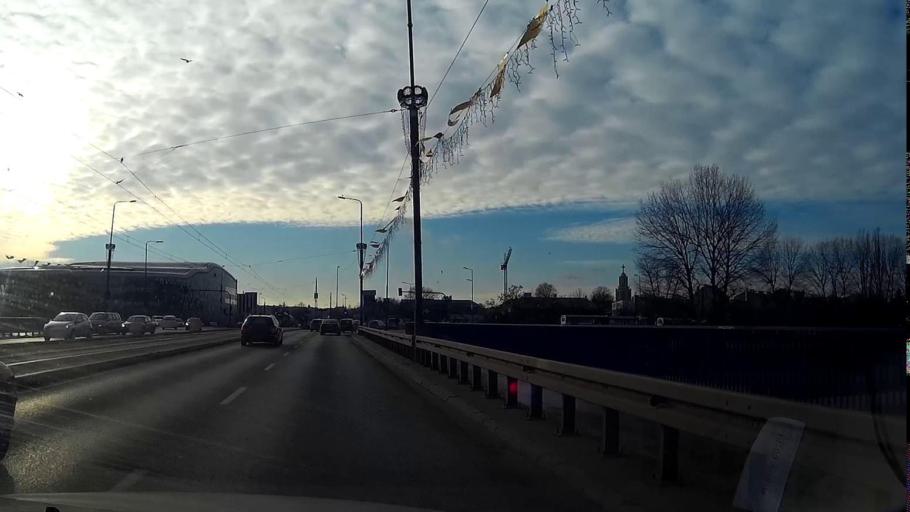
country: PL
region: Lesser Poland Voivodeship
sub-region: Krakow
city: Krakow
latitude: 50.0496
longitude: 19.9339
